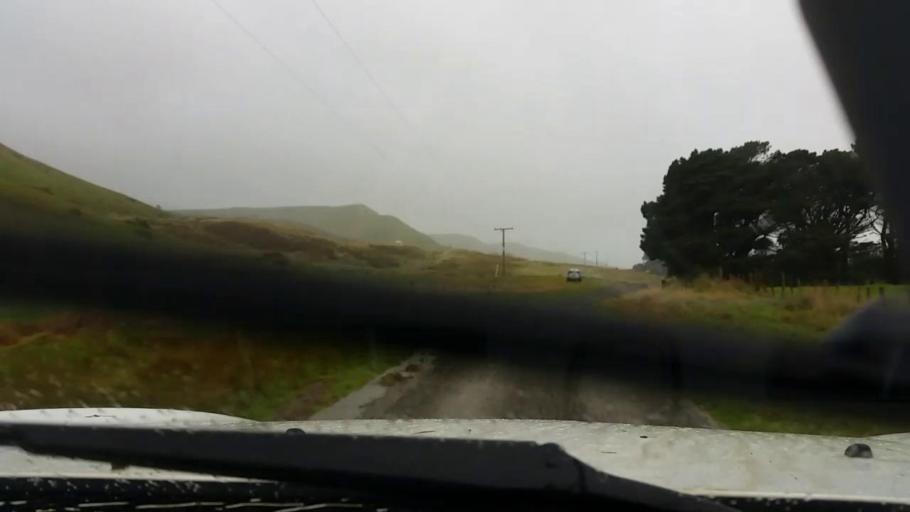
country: NZ
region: Wellington
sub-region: Masterton District
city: Masterton
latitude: -41.2537
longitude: 175.9114
